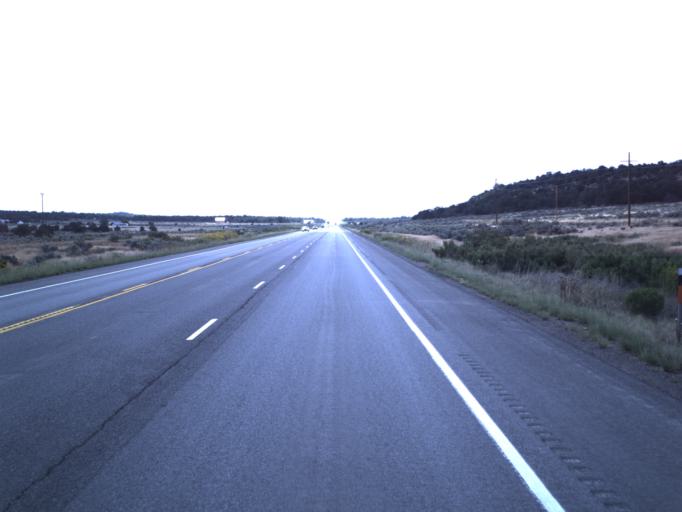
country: US
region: Utah
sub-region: Duchesne County
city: Duchesne
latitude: 40.1800
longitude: -110.6101
